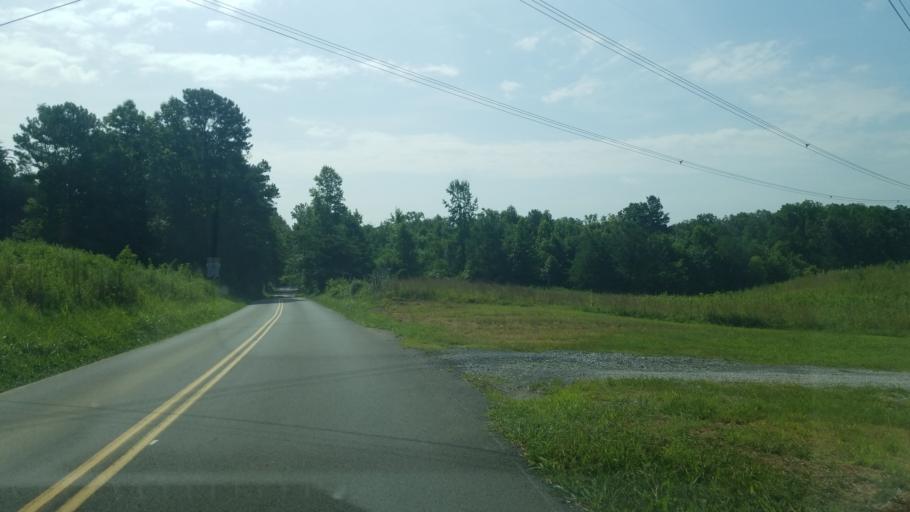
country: US
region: Tennessee
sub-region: Hamilton County
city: Apison
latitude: 35.0728
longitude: -84.9890
